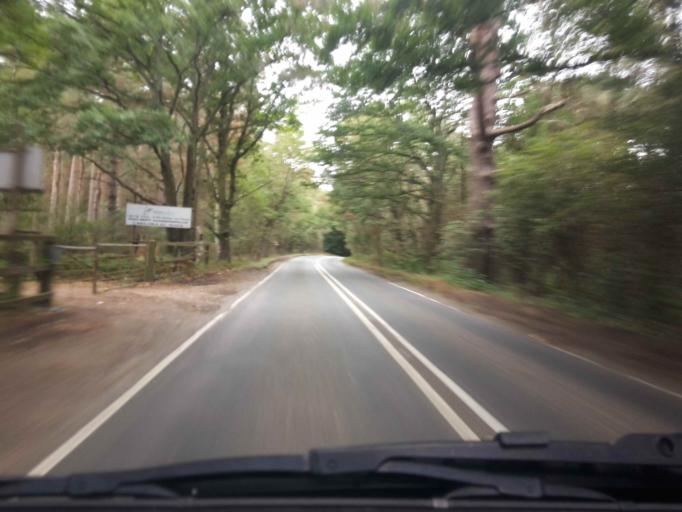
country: GB
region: England
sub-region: Hampshire
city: Eversley
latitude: 51.3359
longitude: -0.8767
